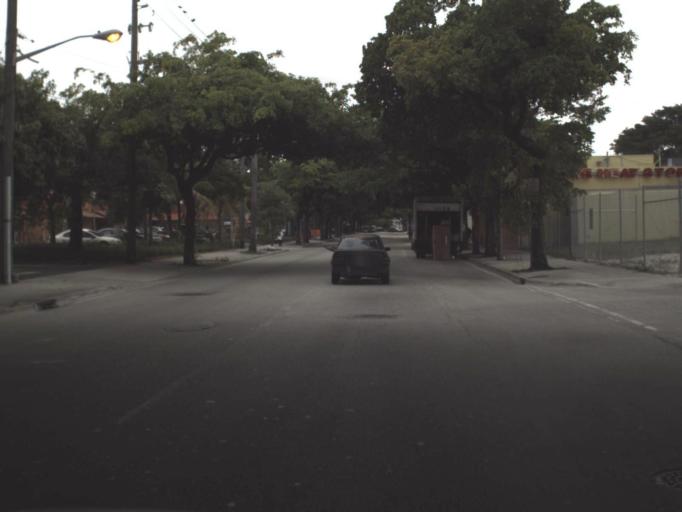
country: US
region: Florida
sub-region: Miami-Dade County
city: Miami
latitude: 25.7887
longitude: -80.1999
